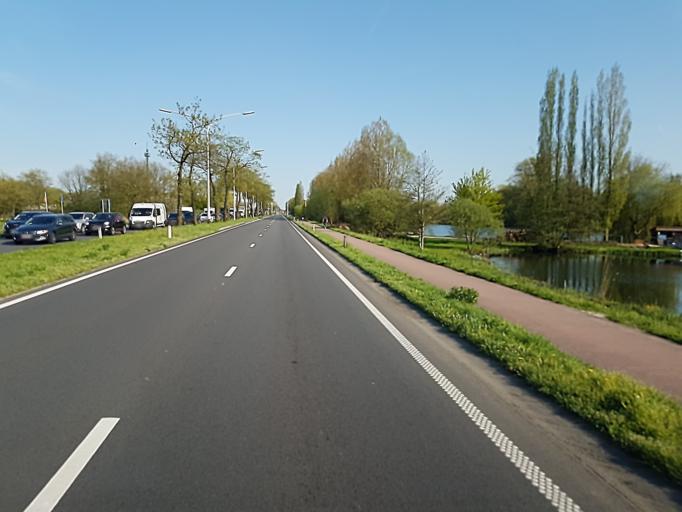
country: BE
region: Flanders
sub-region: Provincie Antwerpen
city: Bornem
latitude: 51.1047
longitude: 4.2384
